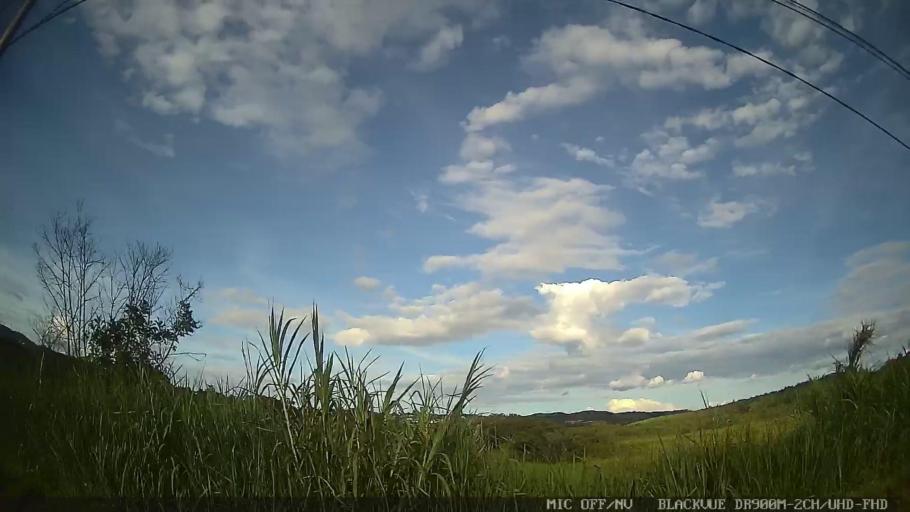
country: BR
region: Sao Paulo
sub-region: Mogi das Cruzes
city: Mogi das Cruzes
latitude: -23.5351
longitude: -46.1546
